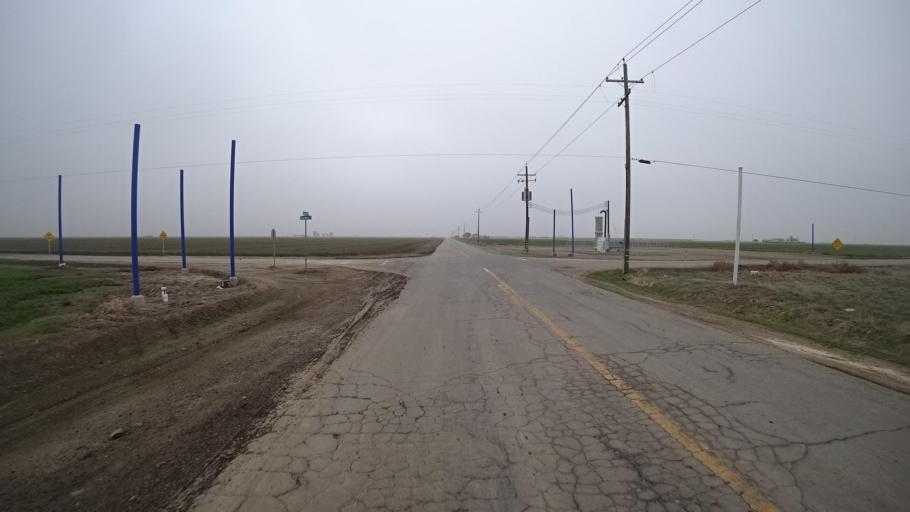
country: US
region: California
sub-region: Kern County
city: Wasco
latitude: 35.6740
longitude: -119.5088
